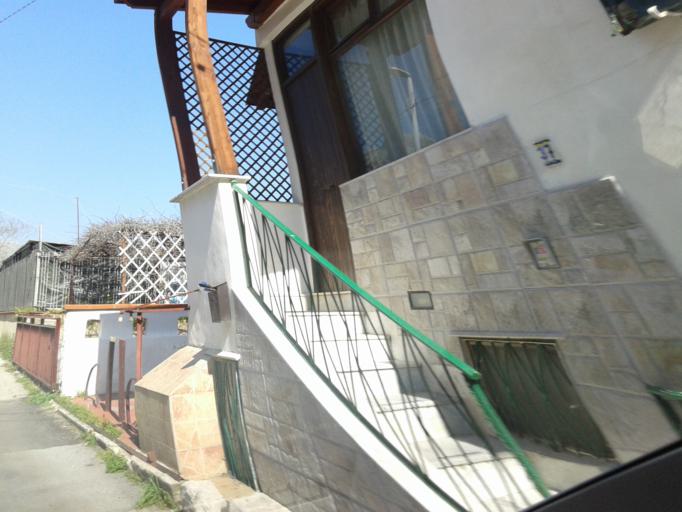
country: IT
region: Sicily
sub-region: Palermo
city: Piano dei Geli
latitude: 38.1105
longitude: 13.2995
